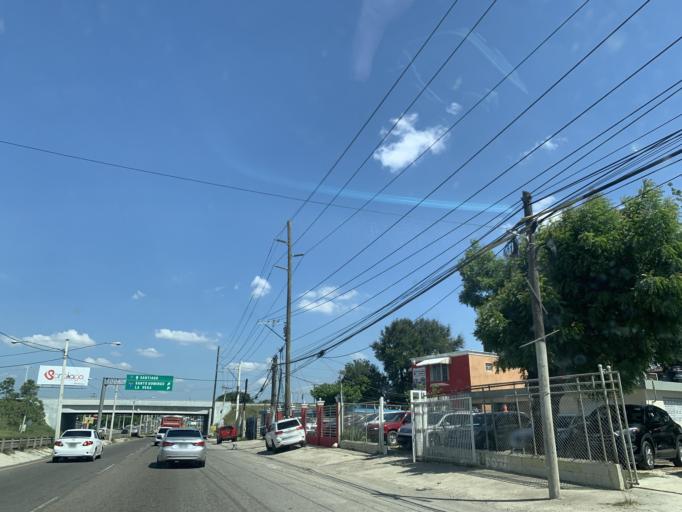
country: DO
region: Santiago
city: Villa Gonzalez
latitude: 19.5184
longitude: -70.7645
